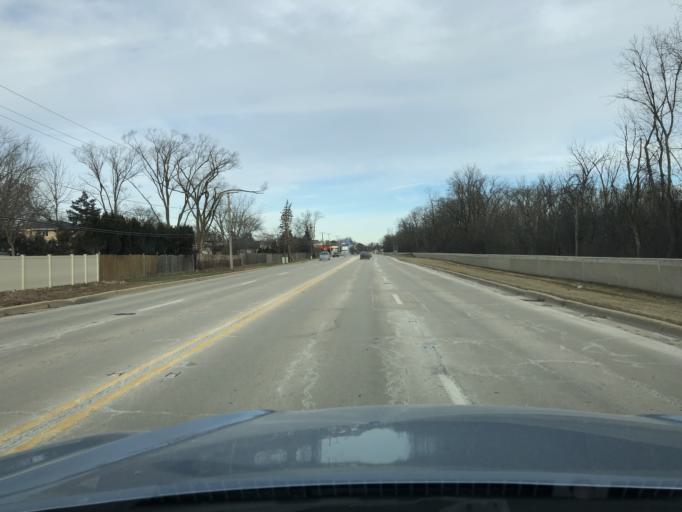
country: US
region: Illinois
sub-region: Cook County
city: Prospect Heights
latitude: 42.0920
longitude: -87.8913
